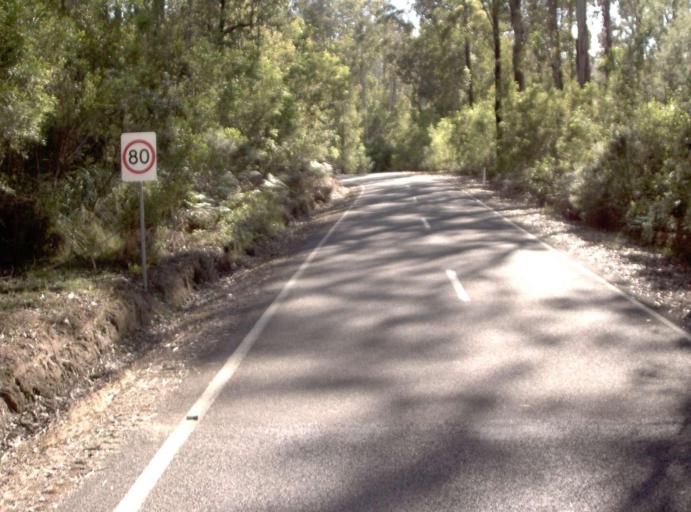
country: AU
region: Victoria
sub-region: East Gippsland
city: Lakes Entrance
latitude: -37.5221
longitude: 148.5330
